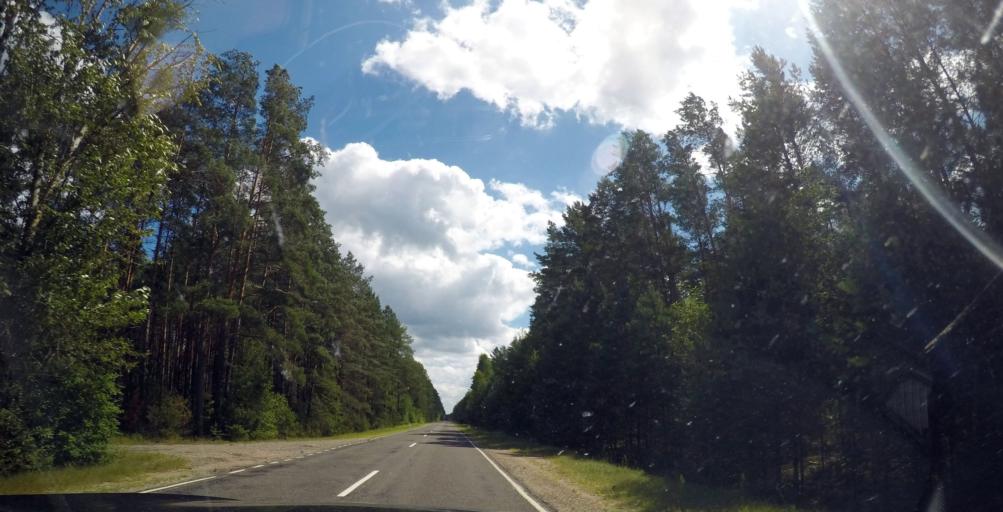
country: LT
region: Alytaus apskritis
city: Druskininkai
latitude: 53.8596
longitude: 24.1802
